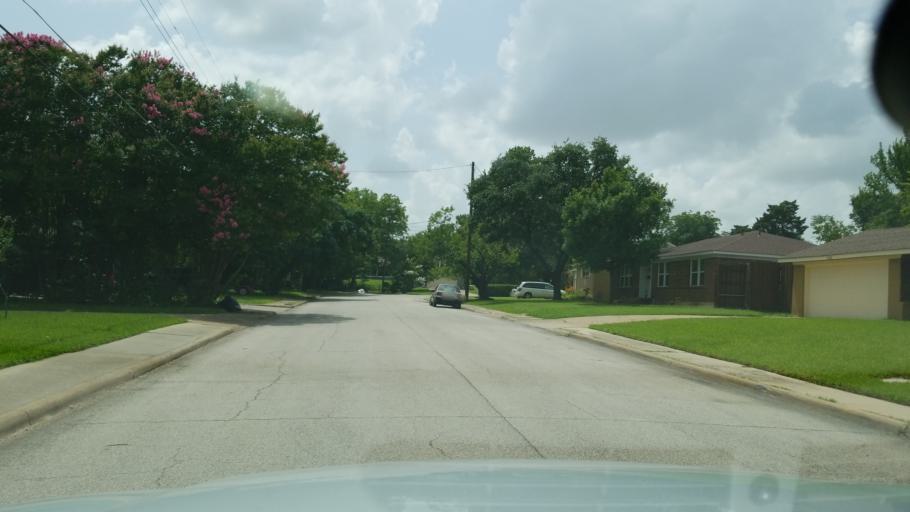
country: US
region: Texas
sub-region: Dallas County
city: Irving
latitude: 32.8230
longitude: -96.9237
